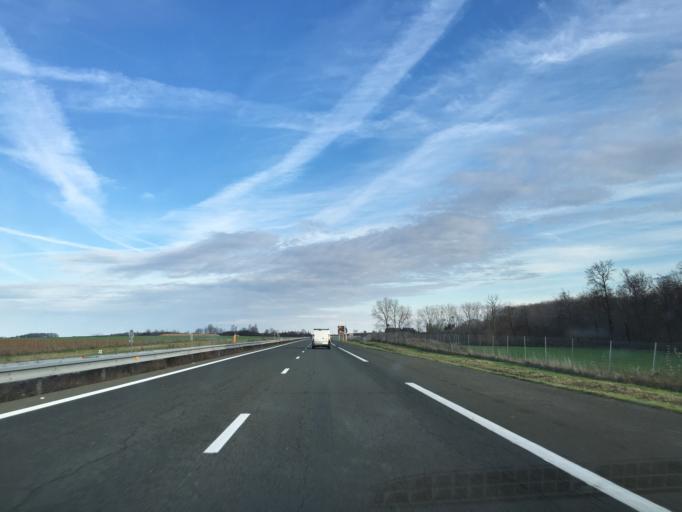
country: FR
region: Picardie
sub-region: Departement de l'Aisne
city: Essomes-sur-Marne
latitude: 49.0652
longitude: 3.3352
